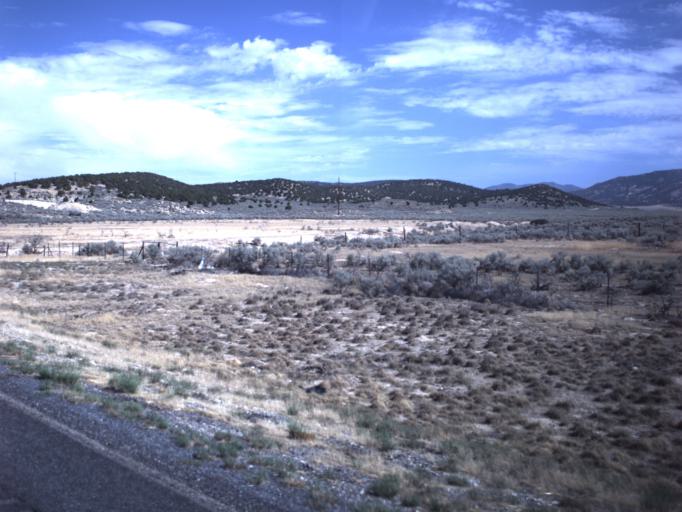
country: US
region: Utah
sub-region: Sanpete County
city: Gunnison
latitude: 39.3188
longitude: -111.9060
